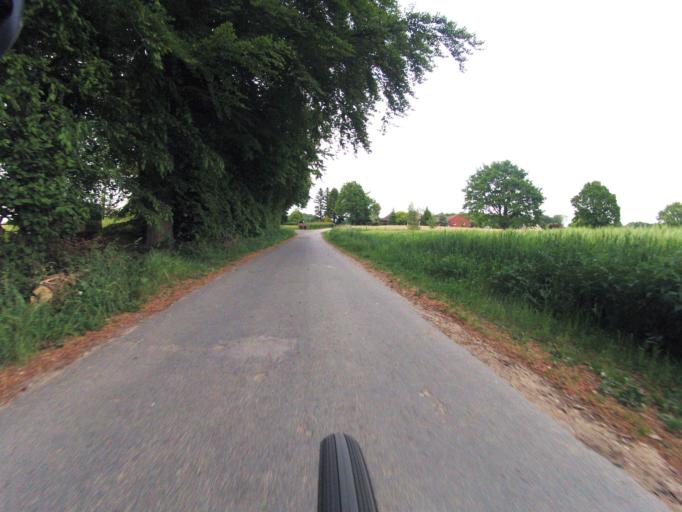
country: DE
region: North Rhine-Westphalia
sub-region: Regierungsbezirk Munster
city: Tecklenburg
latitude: 52.2662
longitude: 7.8056
